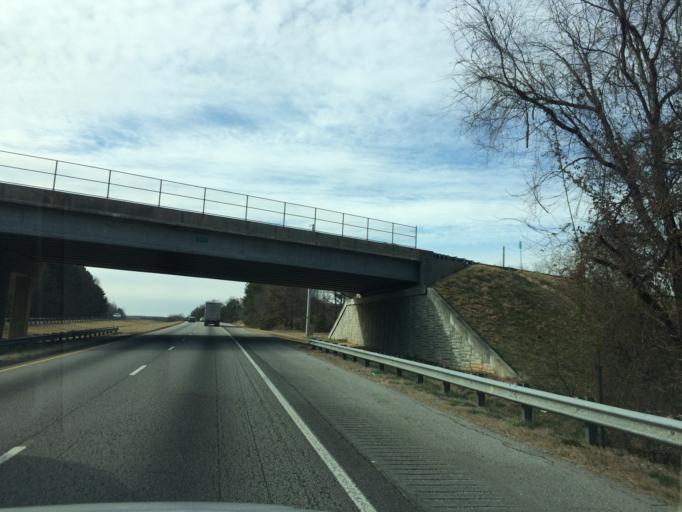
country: US
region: Georgia
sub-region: Jackson County
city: Hoschton
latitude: 34.0974
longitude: -83.8112
